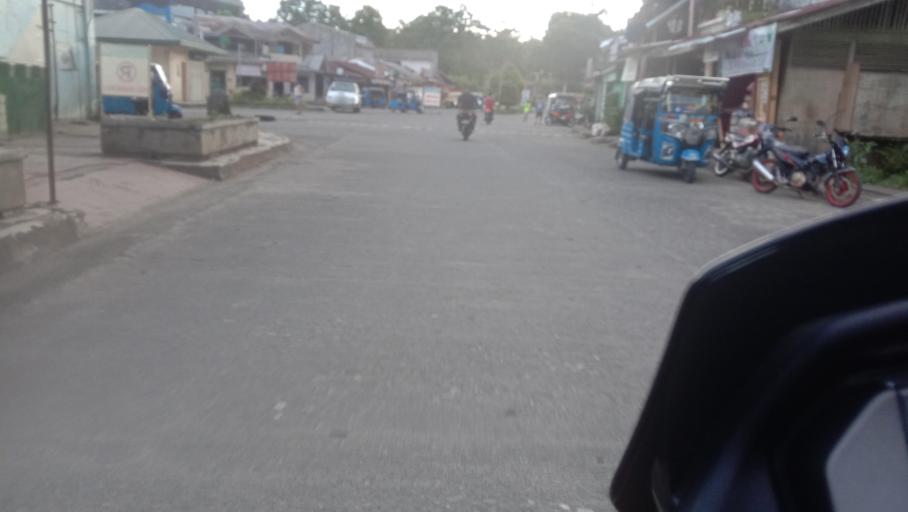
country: PH
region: Caraga
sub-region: Province of Surigao del Sur
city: Barobo
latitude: 8.5275
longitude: 126.1209
